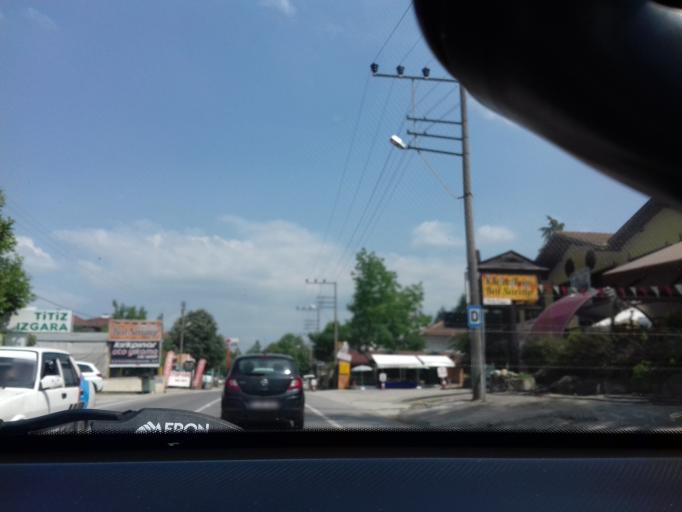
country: TR
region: Sakarya
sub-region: Merkez
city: Sapanca
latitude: 40.6899
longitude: 30.2322
